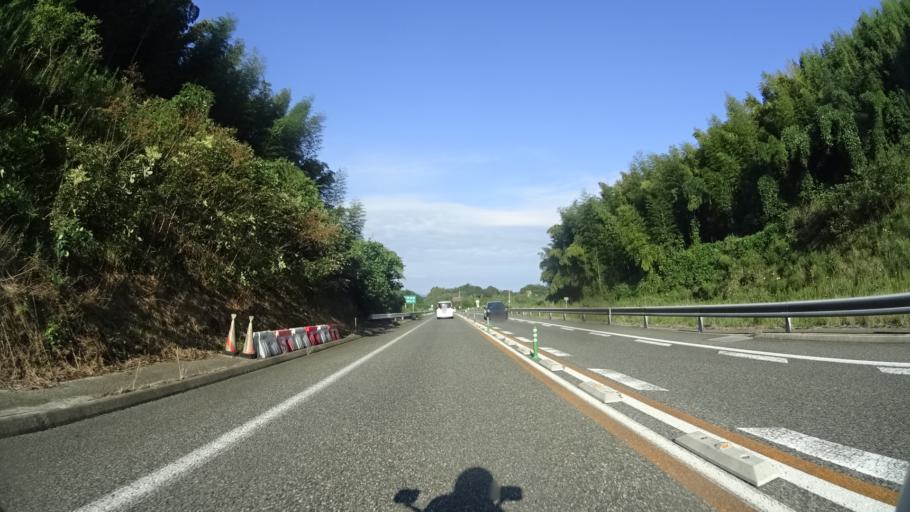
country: JP
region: Shimane
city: Matsue-shi
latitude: 35.4116
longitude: 132.9618
